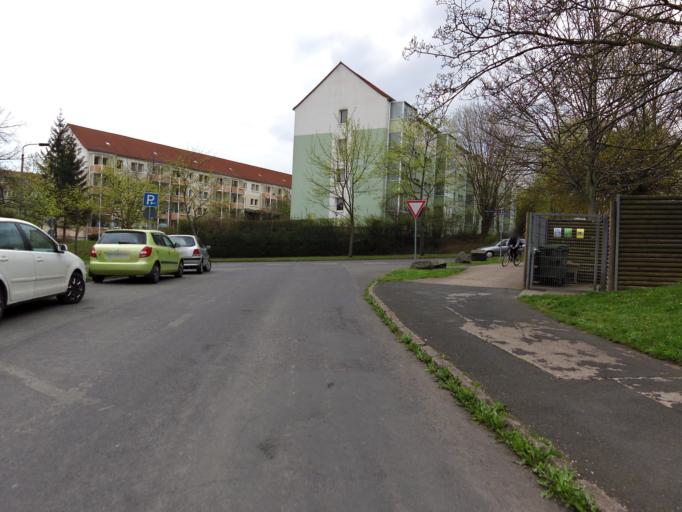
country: DE
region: Thuringia
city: Gotha
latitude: 50.9485
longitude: 10.6848
